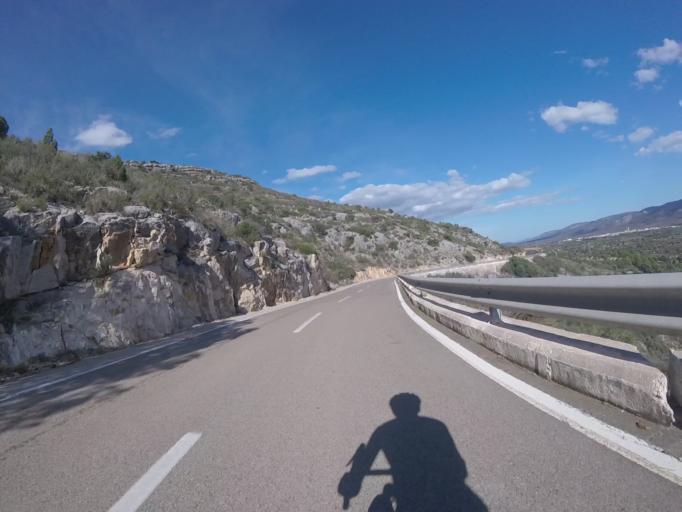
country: ES
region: Valencia
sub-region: Provincia de Castello
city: Alcala de Xivert
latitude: 40.2939
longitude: 0.1838
